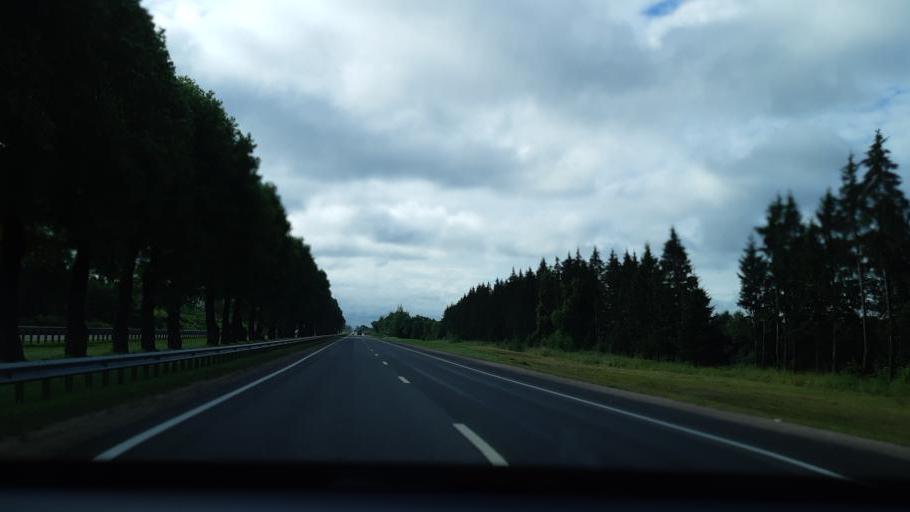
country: RU
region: Smolensk
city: Talashkino
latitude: 54.6909
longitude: 32.1317
